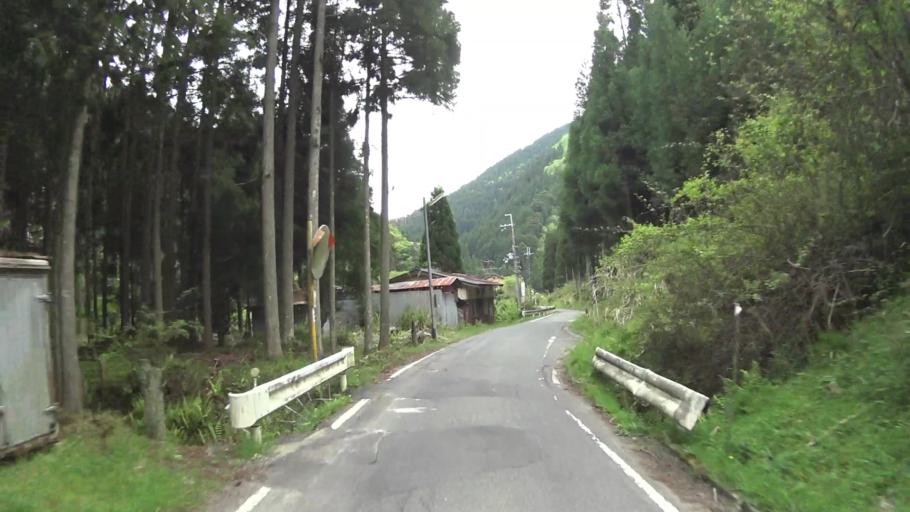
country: JP
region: Kyoto
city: Kameoka
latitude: 35.1233
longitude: 135.6227
